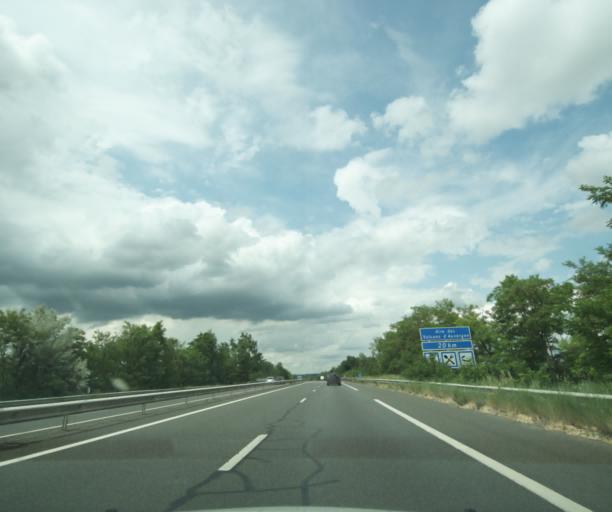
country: FR
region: Auvergne
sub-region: Departement du Puy-de-Dome
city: Riom
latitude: 45.9018
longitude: 3.1544
